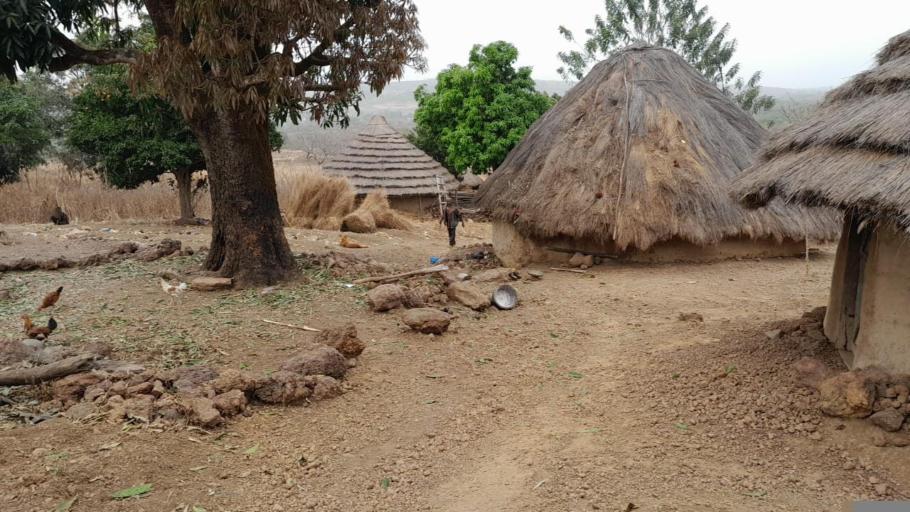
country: GN
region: Mamou
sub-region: Dalaba
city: Dalaba
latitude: 10.8424
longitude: -12.0514
